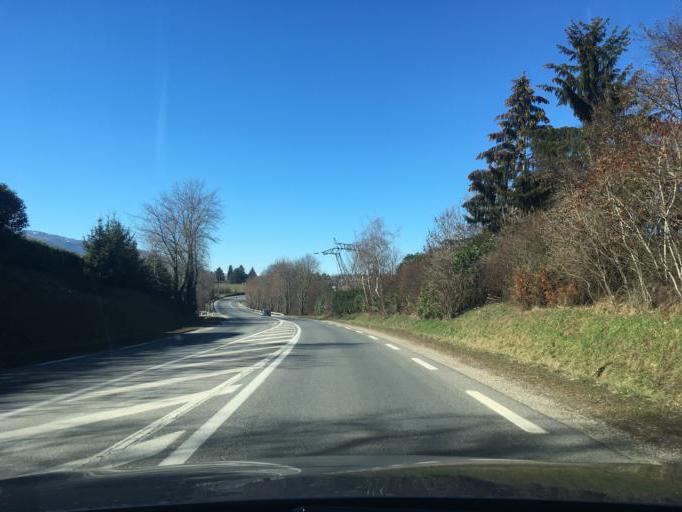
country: FR
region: Rhone-Alpes
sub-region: Departement de la Haute-Savoie
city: Cranves-Sales
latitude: 46.1796
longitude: 6.2946
